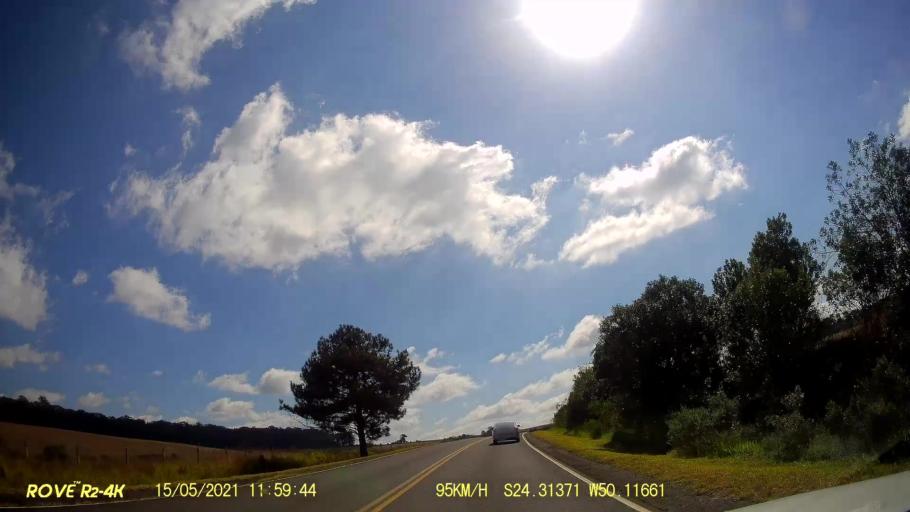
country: BR
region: Parana
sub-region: Pirai Do Sul
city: Pirai do Sul
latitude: -24.3136
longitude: -50.1165
